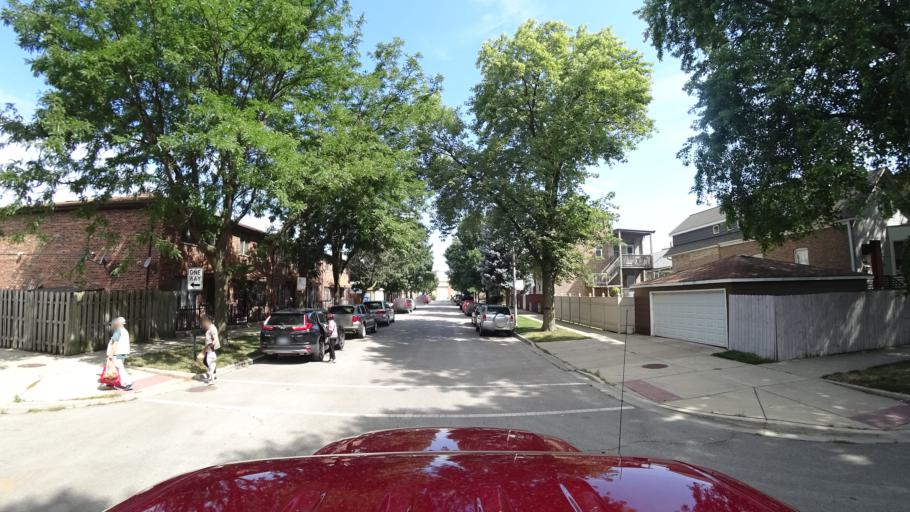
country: US
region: Illinois
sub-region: Cook County
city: Chicago
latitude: 41.8297
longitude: -87.6477
